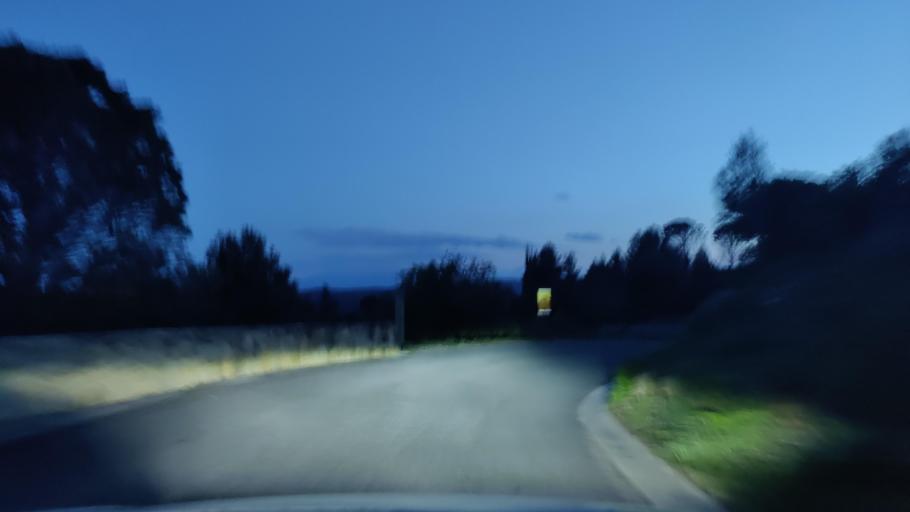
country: FR
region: Languedoc-Roussillon
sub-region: Departement des Pyrenees-Orientales
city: Estagel
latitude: 42.8797
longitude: 2.7451
